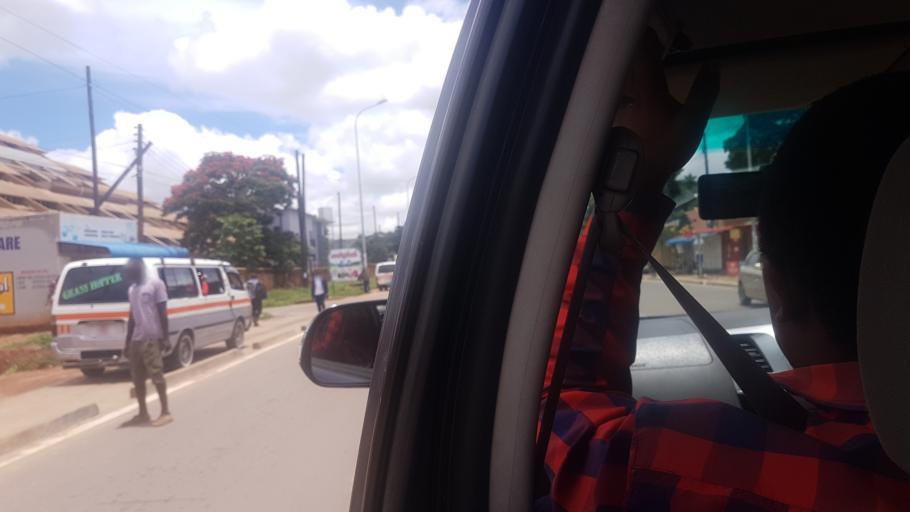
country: ZM
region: Lusaka
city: Lusaka
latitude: -15.4314
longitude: 28.3120
